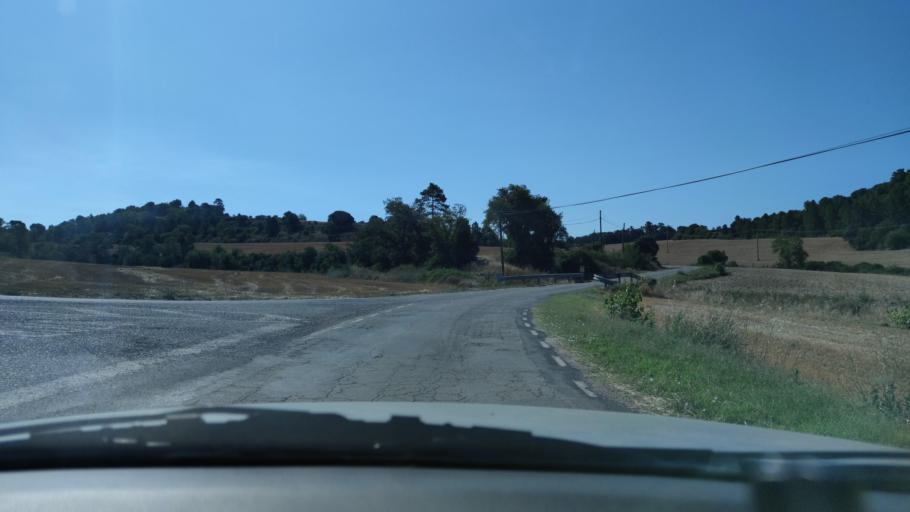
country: ES
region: Catalonia
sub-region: Provincia de Lleida
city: Sant Guim de Freixenet
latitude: 41.6860
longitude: 1.3955
